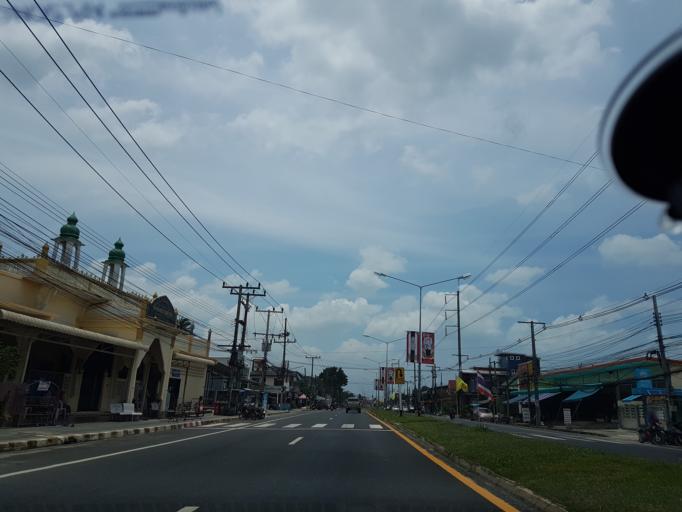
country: TH
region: Songkhla
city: Songkhla
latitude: 7.1041
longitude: 100.6332
